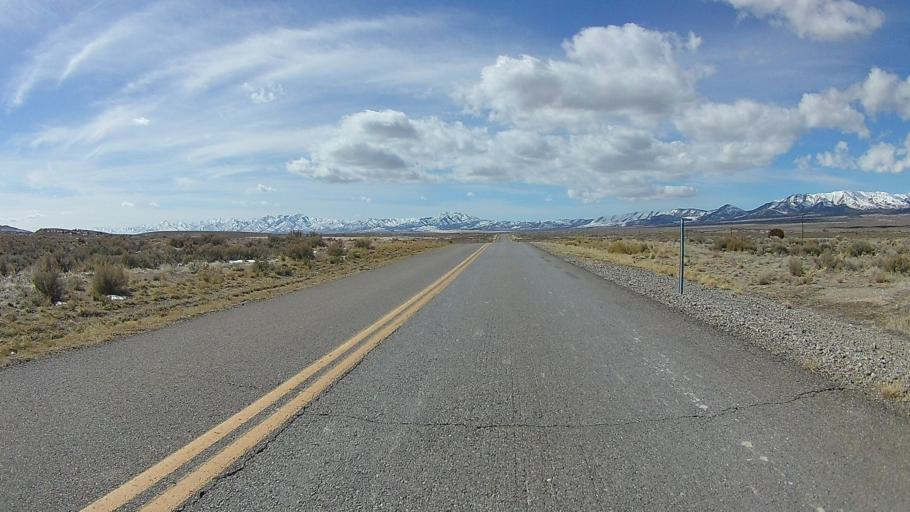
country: US
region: Utah
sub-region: Tooele County
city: Tooele
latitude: 40.1796
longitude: -112.3981
